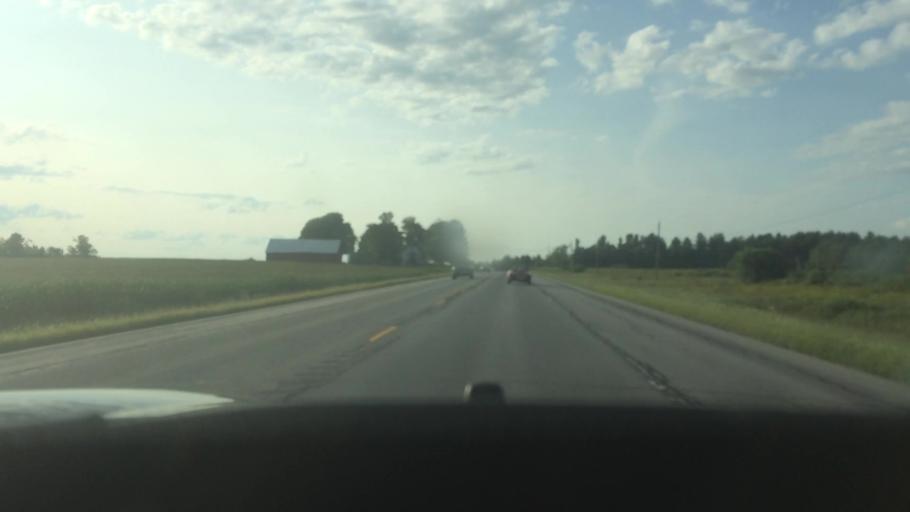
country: US
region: New York
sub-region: St. Lawrence County
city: Canton
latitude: 44.6267
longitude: -75.2372
